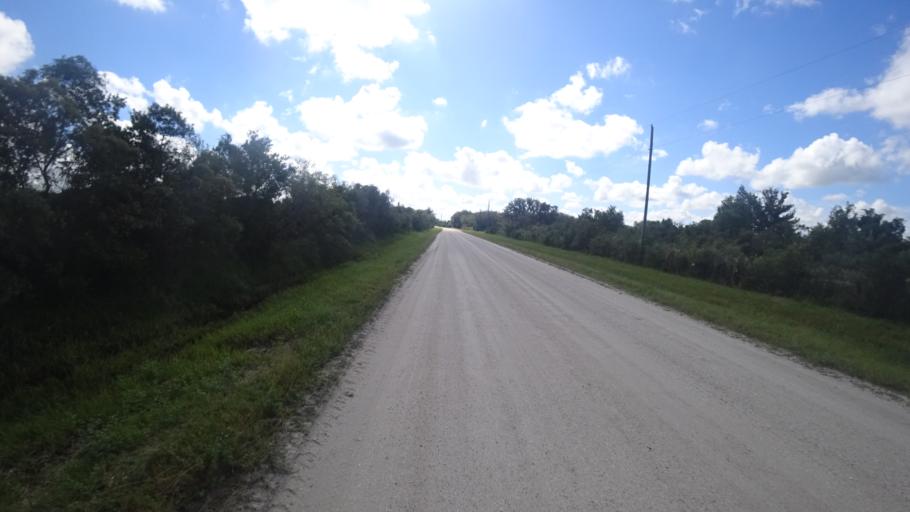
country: US
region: Florida
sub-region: Sarasota County
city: Lake Sarasota
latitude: 27.3626
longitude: -82.1339
